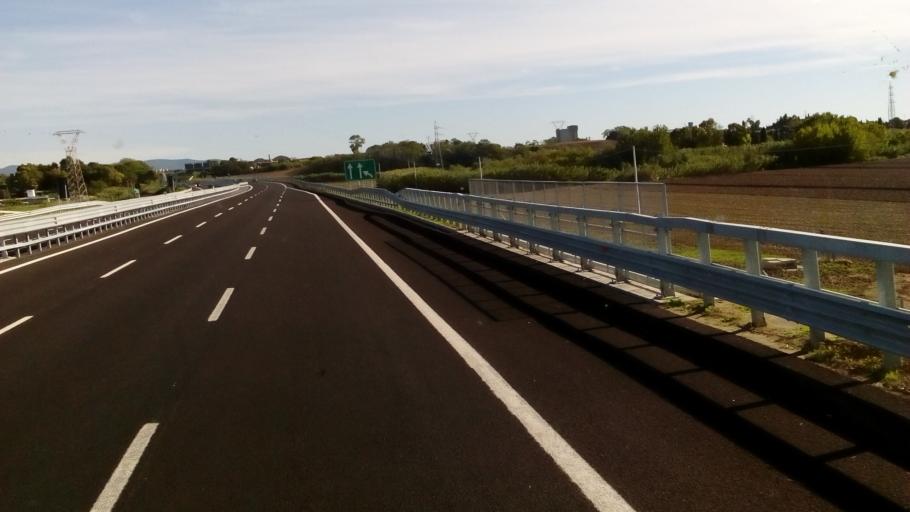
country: IT
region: Latium
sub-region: Provincia di Viterbo
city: Tarquinia
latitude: 42.2538
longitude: 11.7303
